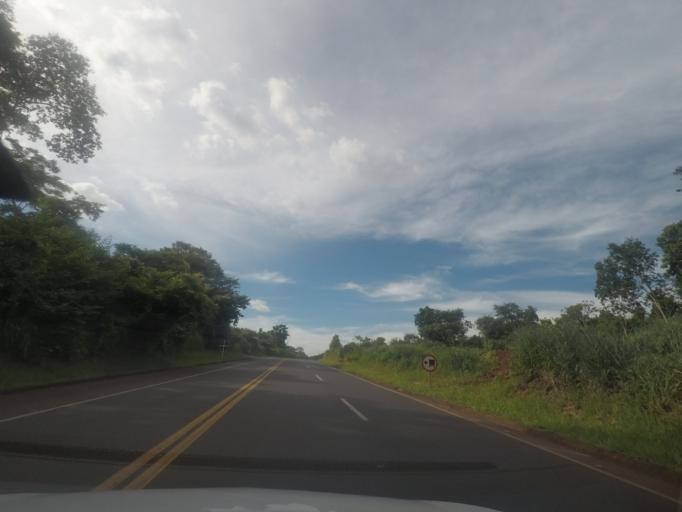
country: BR
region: Minas Gerais
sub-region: Monte Alegre De Minas
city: Monte Alegre de Minas
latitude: -19.0380
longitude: -49.0113
